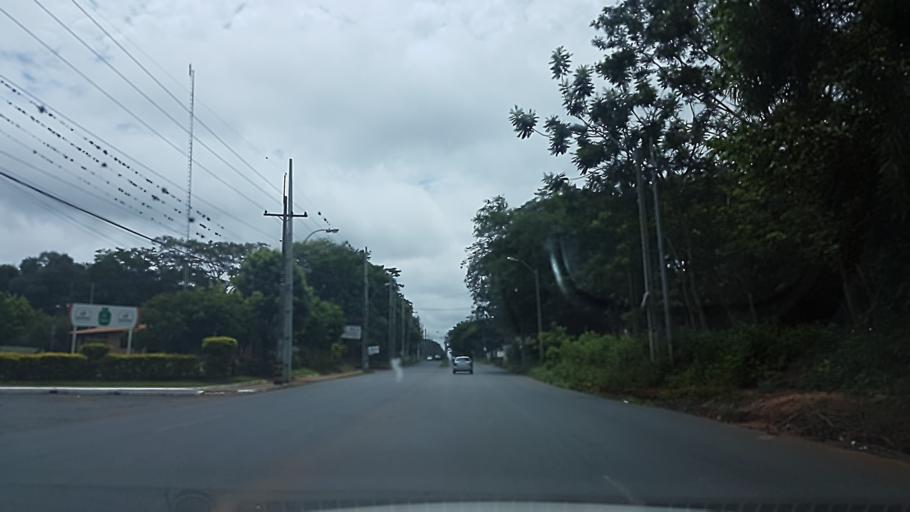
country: PY
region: Central
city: Villa Elisa
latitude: -25.3995
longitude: -57.5769
